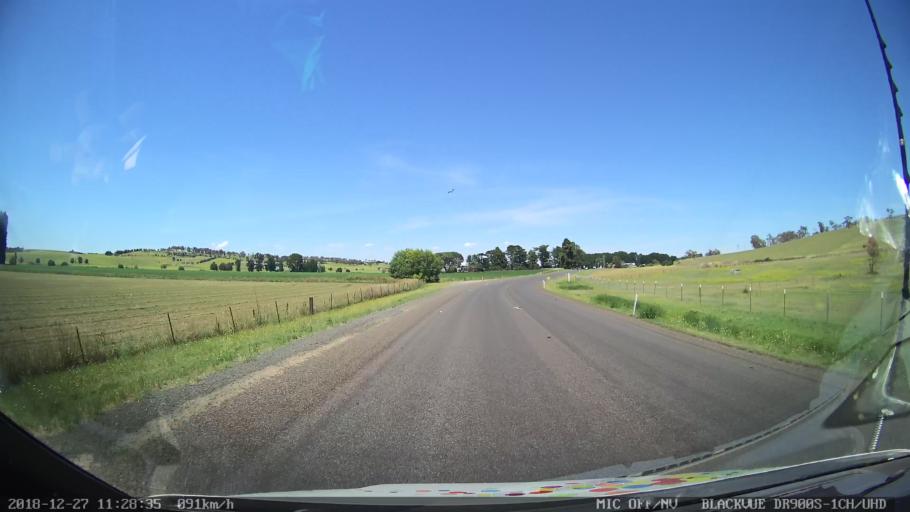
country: AU
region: New South Wales
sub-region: Bathurst Regional
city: Perthville
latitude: -33.4783
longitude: 149.5625
